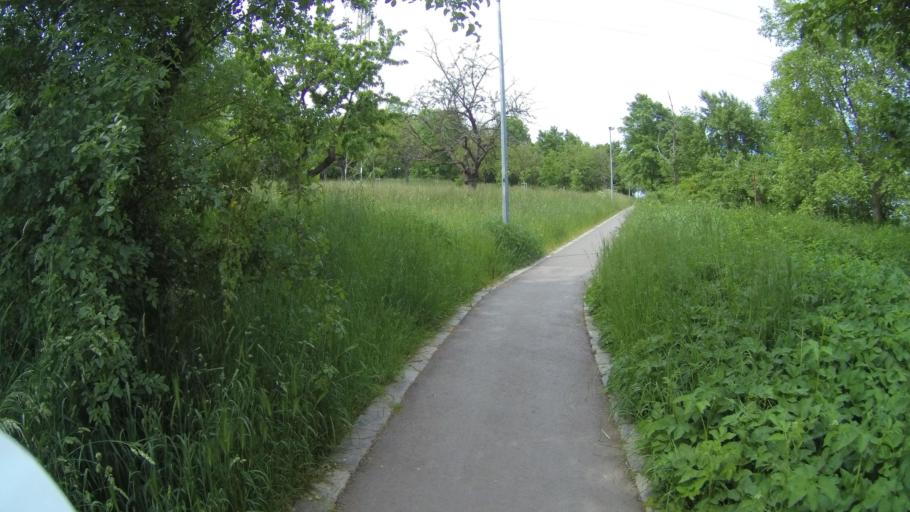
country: CZ
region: Praha
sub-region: Praha 9
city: Strizkov
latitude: 50.1398
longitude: 14.4776
